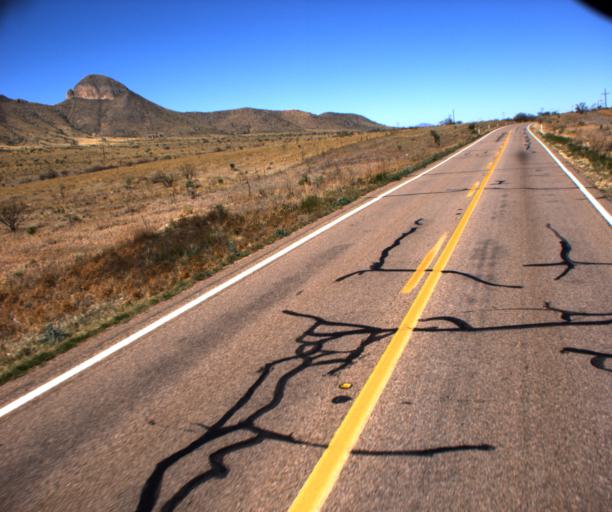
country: US
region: Arizona
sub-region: Cochise County
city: Huachuca City
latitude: 31.7160
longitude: -110.4673
